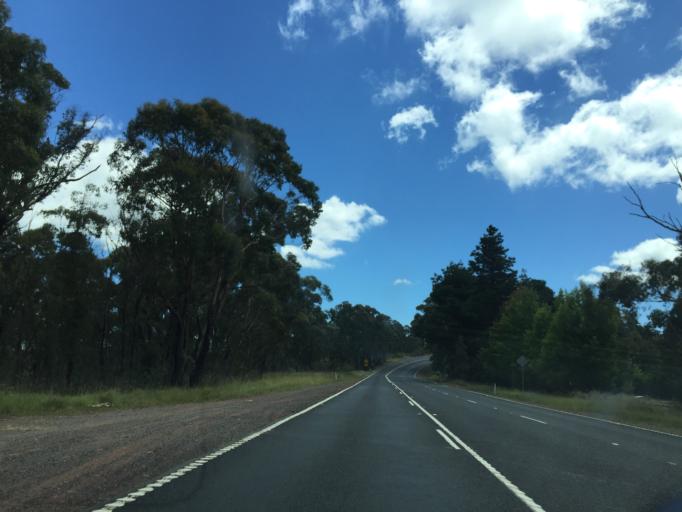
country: AU
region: New South Wales
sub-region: Blue Mountains Municipality
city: Blackheath
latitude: -33.5188
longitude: 150.2994
